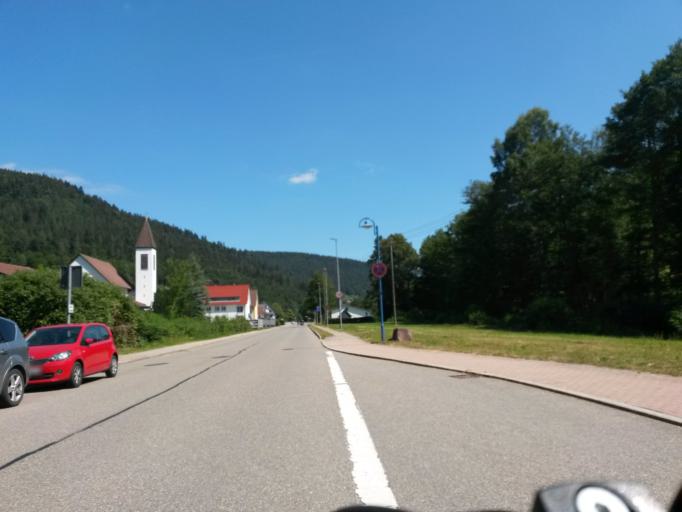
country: DE
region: Baden-Wuerttemberg
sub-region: Karlsruhe Region
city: Enzklosterle
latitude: 48.6679
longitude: 8.4748
